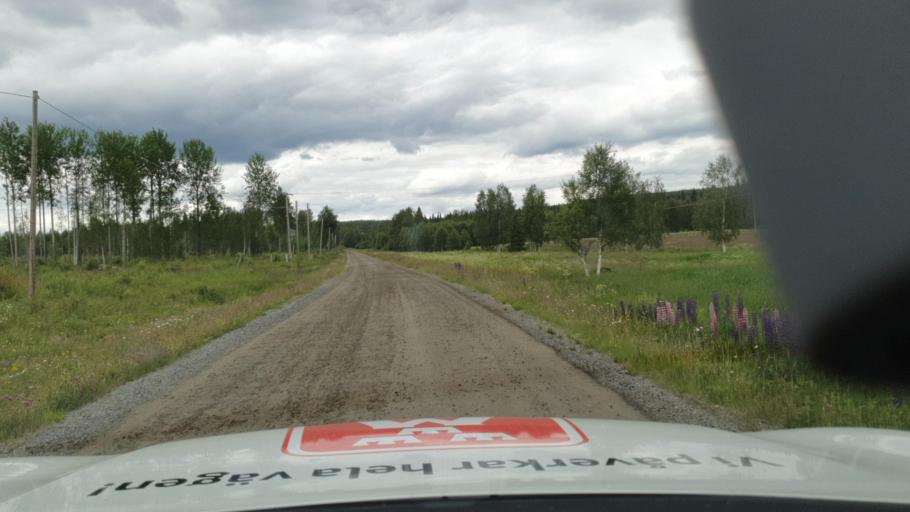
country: SE
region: Vaesterbotten
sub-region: Bjurholms Kommun
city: Bjurholm
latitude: 63.7987
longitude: 19.0858
